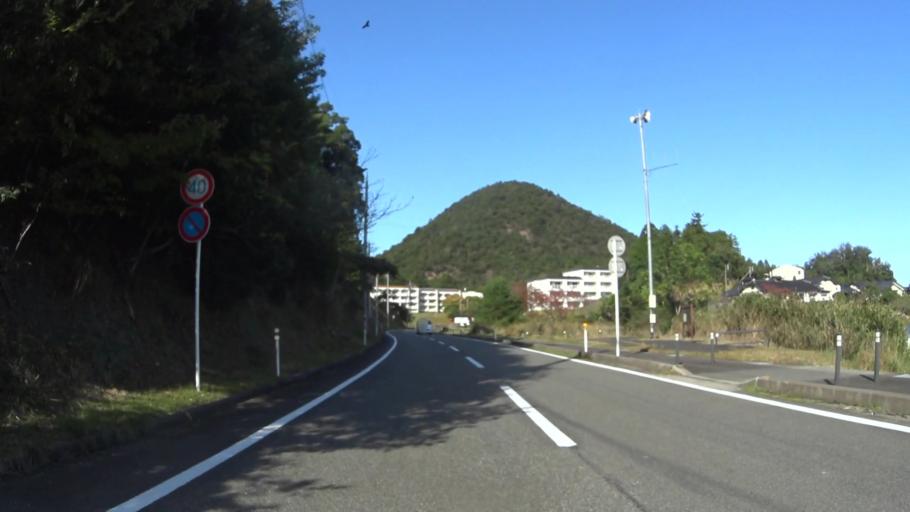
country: JP
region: Hyogo
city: Toyooka
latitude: 35.6337
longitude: 134.8886
